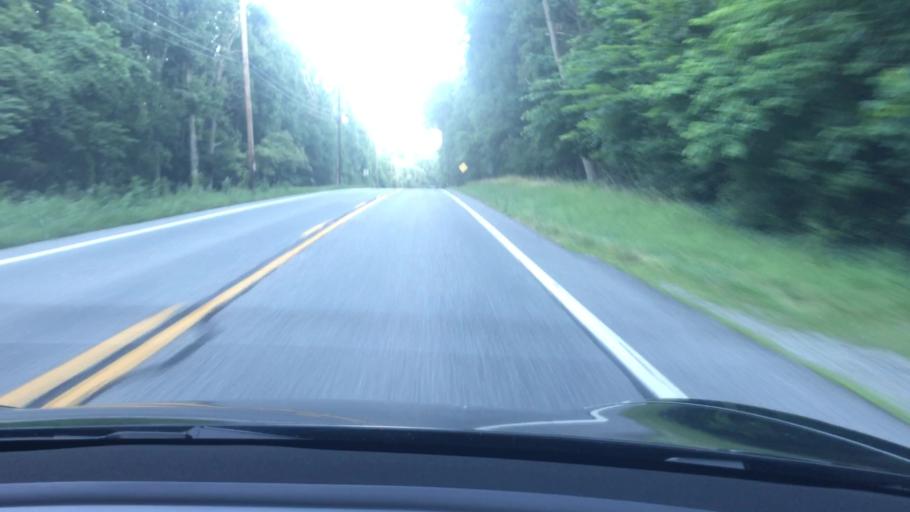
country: US
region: Pennsylvania
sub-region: York County
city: Dover
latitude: 40.0943
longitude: -76.8709
